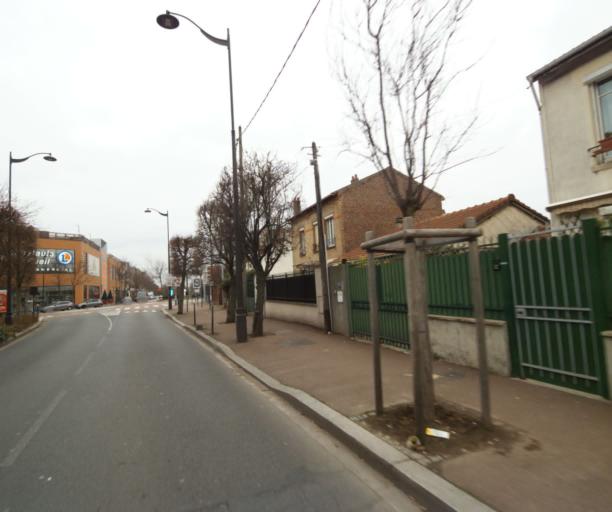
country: FR
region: Ile-de-France
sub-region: Departement des Hauts-de-Seine
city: Rueil-Malmaison
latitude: 48.8620
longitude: 2.1970
